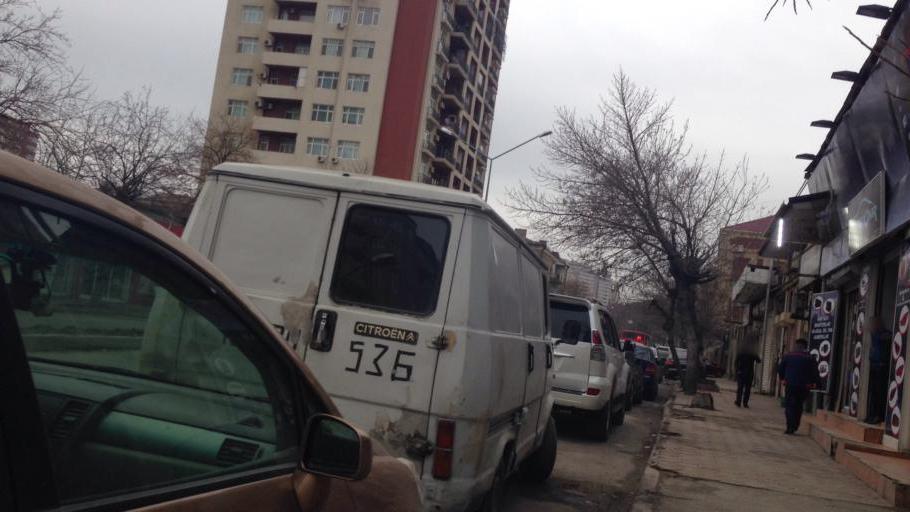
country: AZ
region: Baki
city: Baku
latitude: 40.3900
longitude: 49.8546
